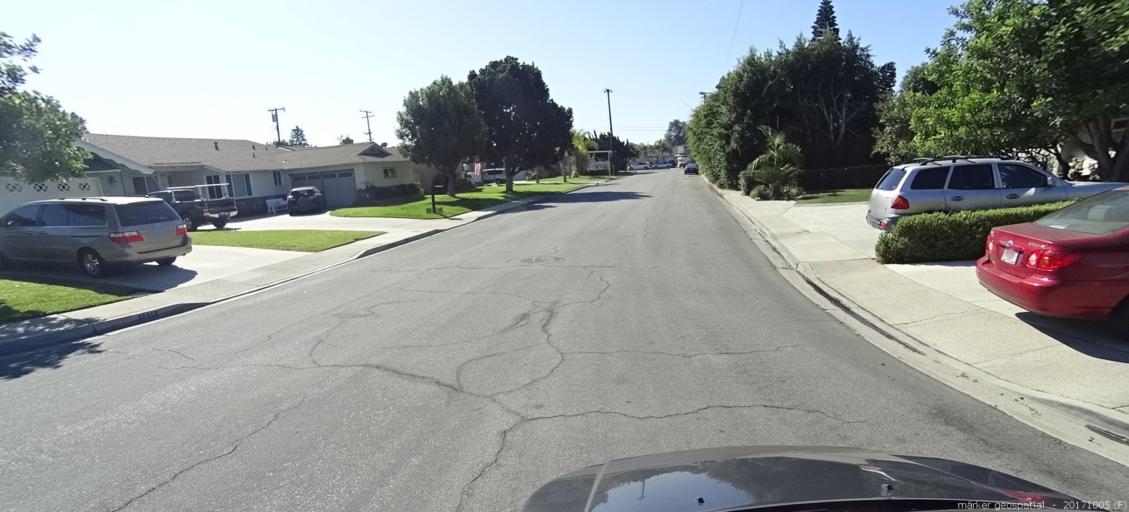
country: US
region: California
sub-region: Orange County
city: Stanton
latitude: 33.8008
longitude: -117.9665
